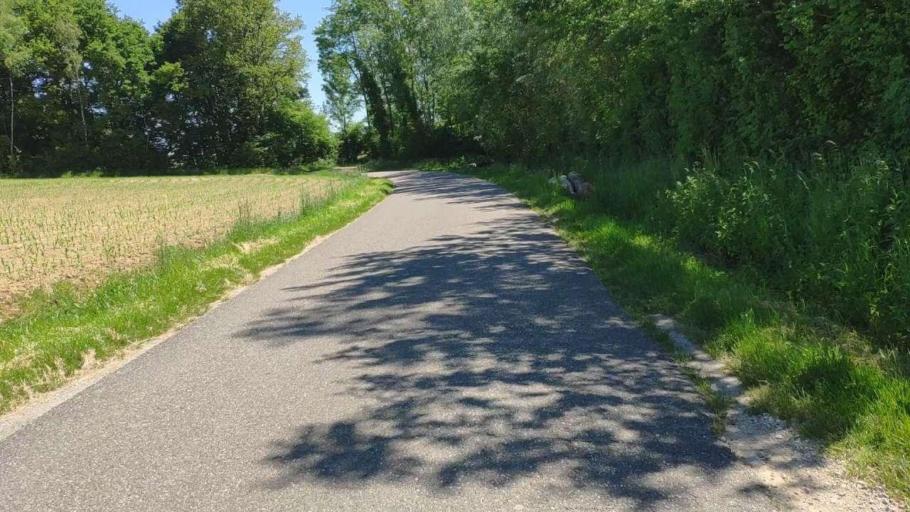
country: FR
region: Franche-Comte
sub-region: Departement du Jura
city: Bletterans
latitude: 46.7644
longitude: 5.4254
